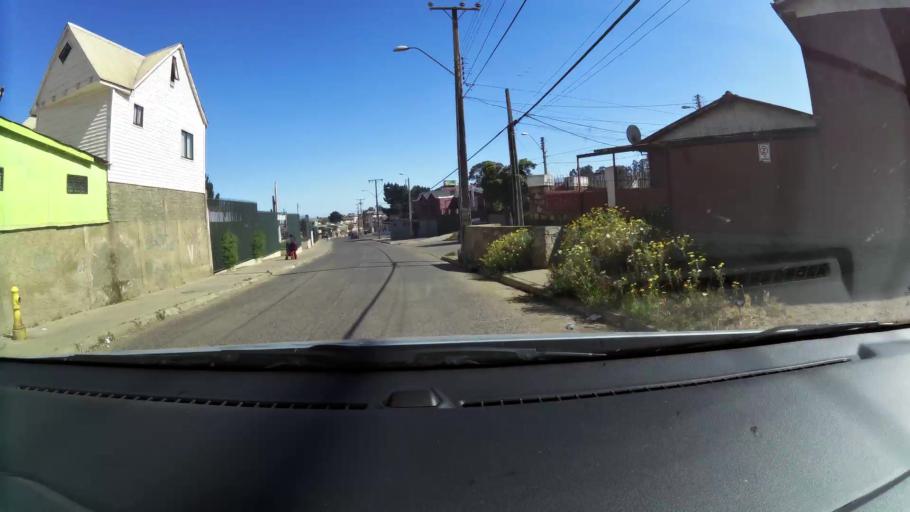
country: CL
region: Valparaiso
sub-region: Provincia de Valparaiso
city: Valparaiso
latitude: -33.0540
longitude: -71.6510
